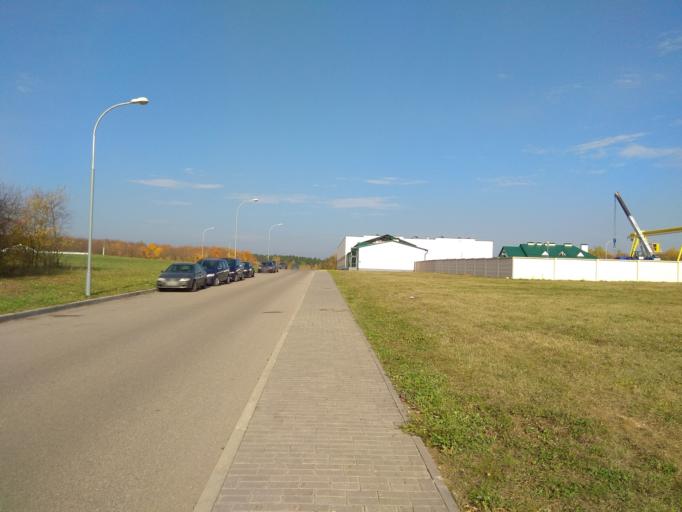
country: BY
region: Grodnenskaya
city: Hrodna
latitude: 53.7095
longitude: 23.7982
